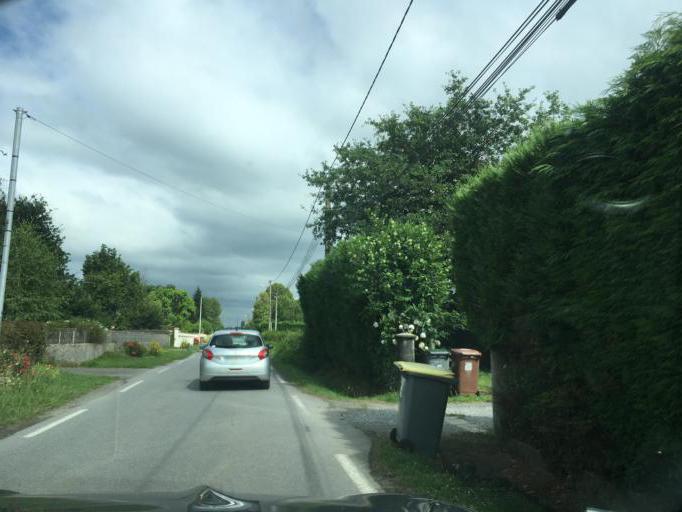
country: FR
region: Aquitaine
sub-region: Departement des Pyrenees-Atlantiques
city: Ousse
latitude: 43.3124
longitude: -0.2798
